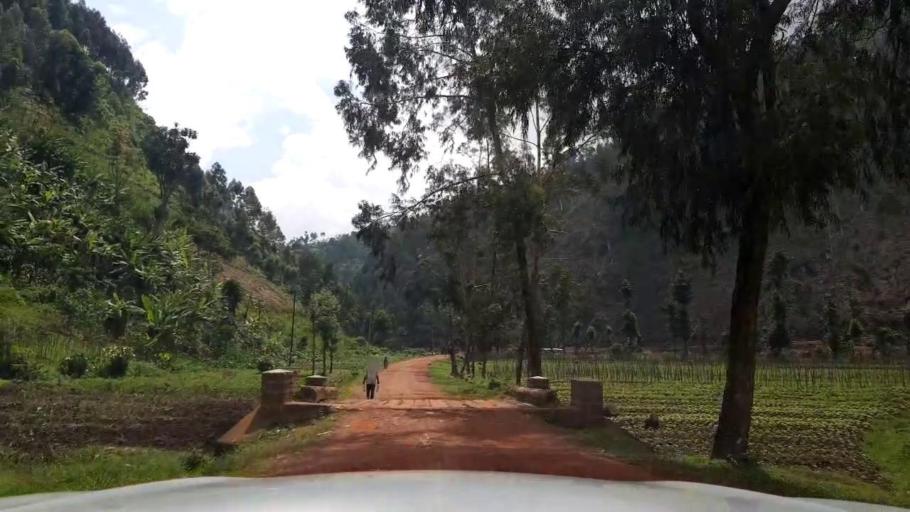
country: UG
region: Western Region
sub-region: Kisoro District
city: Kisoro
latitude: -1.3835
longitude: 29.7977
